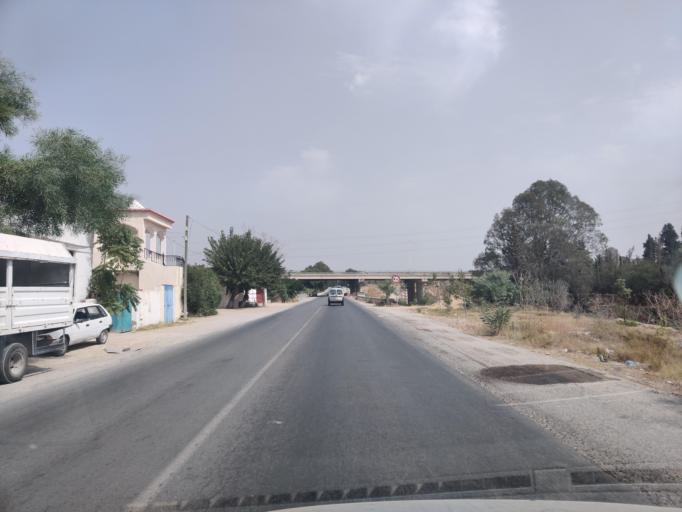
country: TN
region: Nabul
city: Al Hammamat
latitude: 36.4398
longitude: 10.5733
